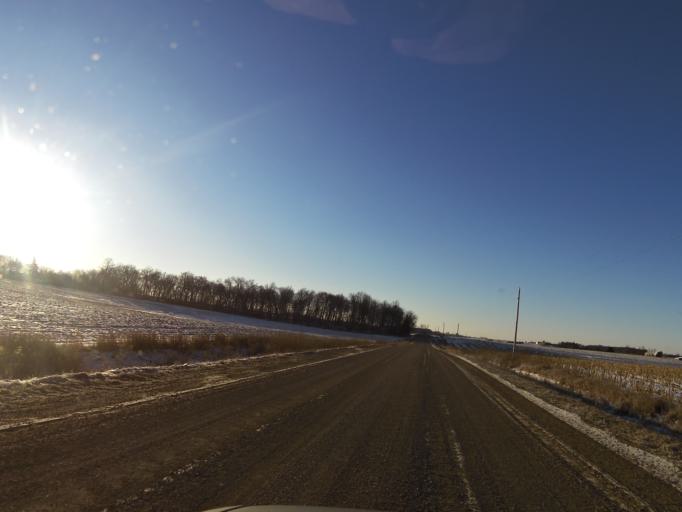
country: US
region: Minnesota
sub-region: Scott County
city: Jordan
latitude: 44.6693
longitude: -93.5420
